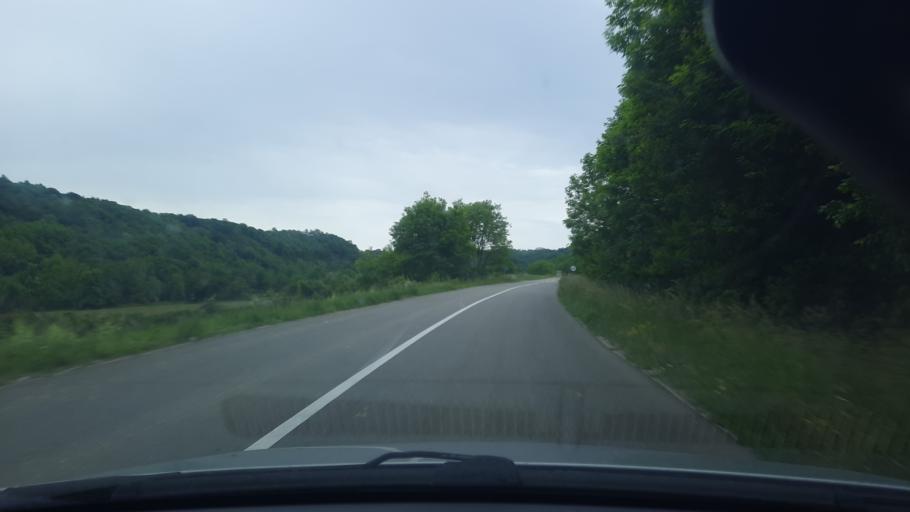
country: RS
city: Bukor
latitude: 44.5235
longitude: 19.5138
